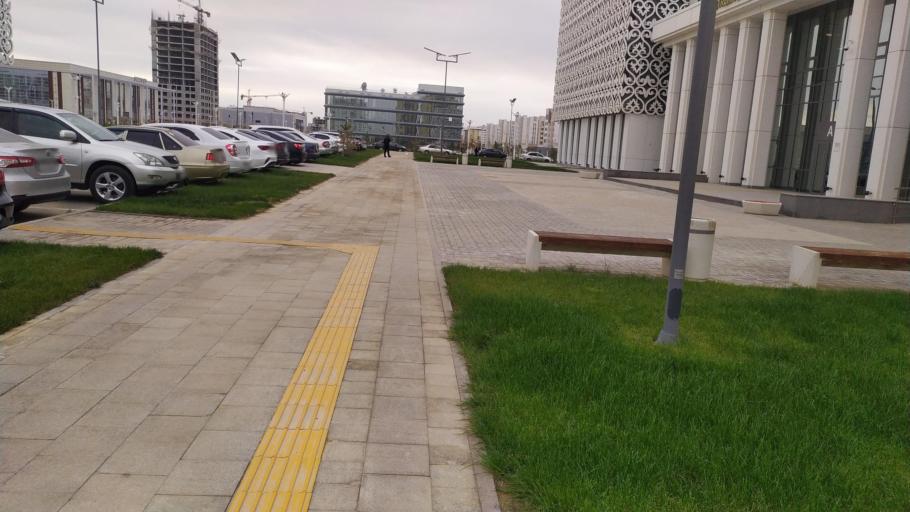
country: KZ
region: Ongtustik Qazaqstan
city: Turkestan
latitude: 43.2780
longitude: 68.3492
